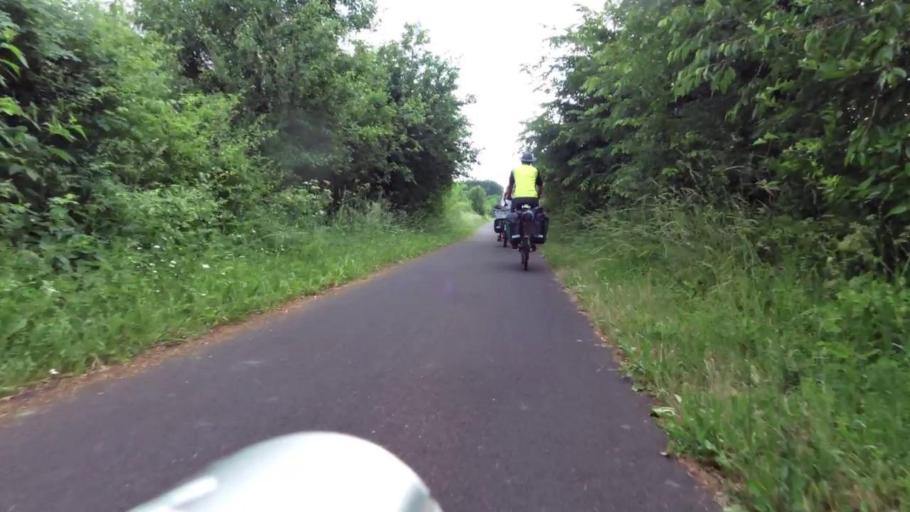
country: PL
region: Kujawsko-Pomorskie
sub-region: Powiat torunski
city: Lubianka
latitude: 53.1118
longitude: 18.4871
